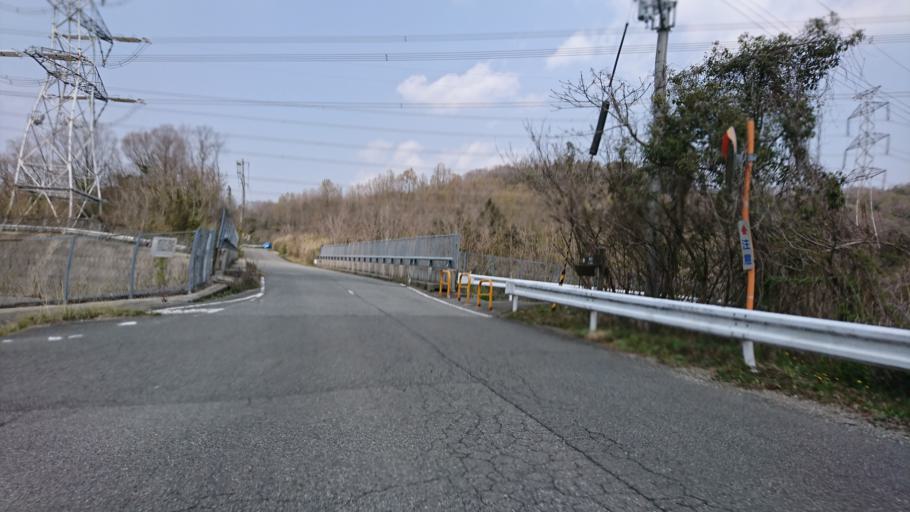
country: JP
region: Hyogo
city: Ono
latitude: 34.8216
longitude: 134.9038
